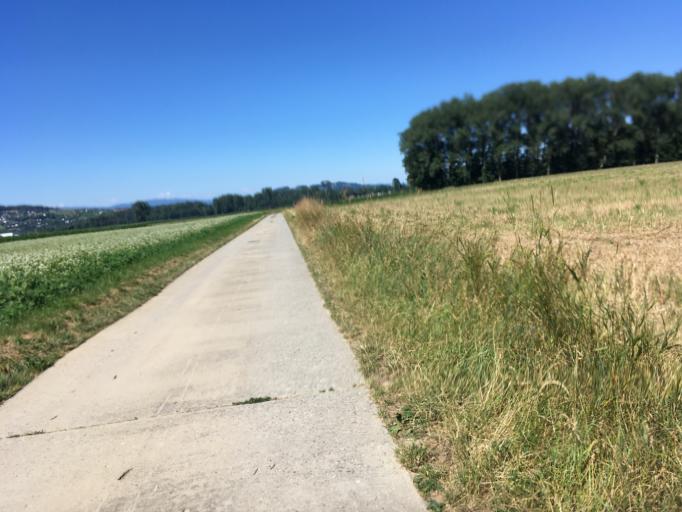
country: CH
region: Vaud
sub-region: Broye-Vully District
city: Avenches
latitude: 46.8969
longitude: 7.0250
